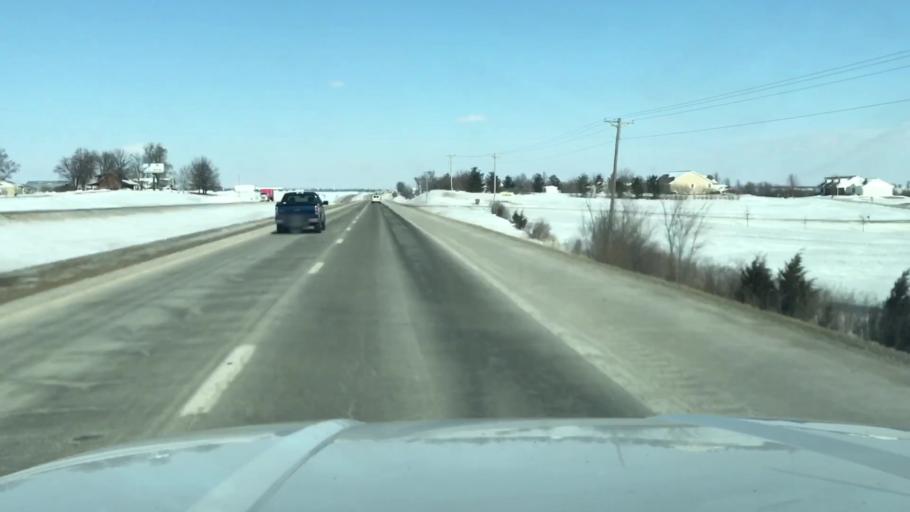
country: US
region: Missouri
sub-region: Nodaway County
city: Maryville
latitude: 40.2882
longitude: -94.8753
